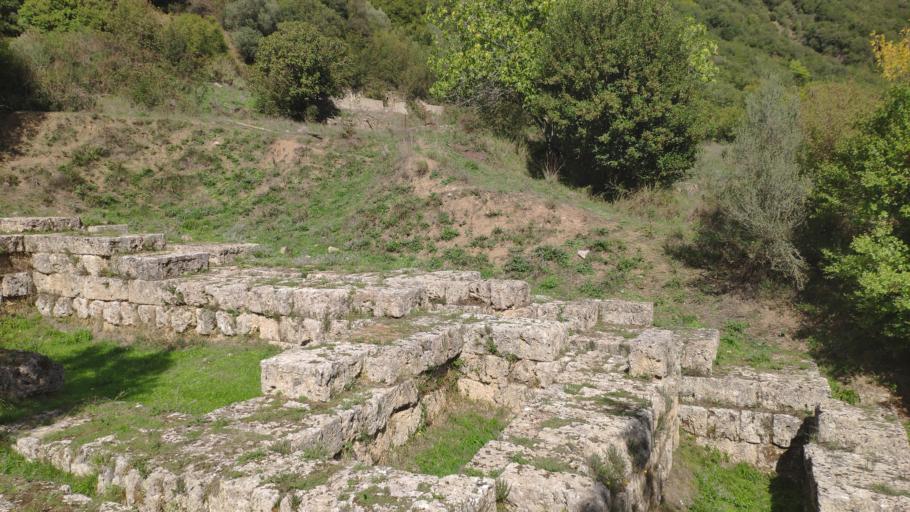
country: GR
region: Peloponnese
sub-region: Nomos Arkadias
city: Dimitsana
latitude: 37.5397
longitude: 22.0453
